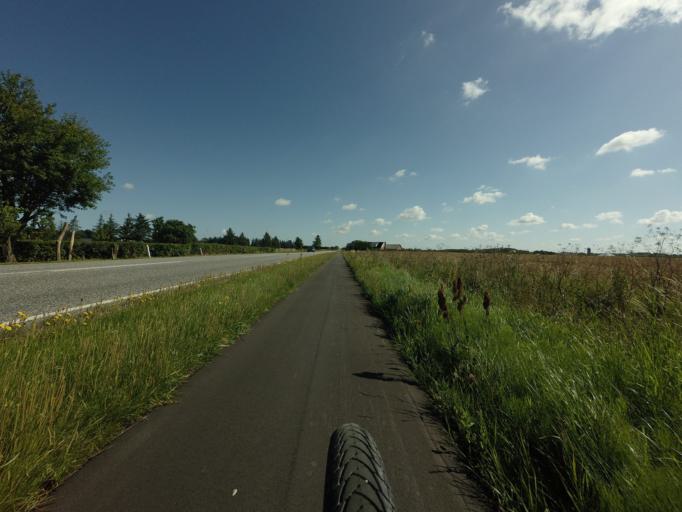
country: DK
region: North Denmark
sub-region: Hjorring Kommune
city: Vra
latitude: 57.4136
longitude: 9.8205
